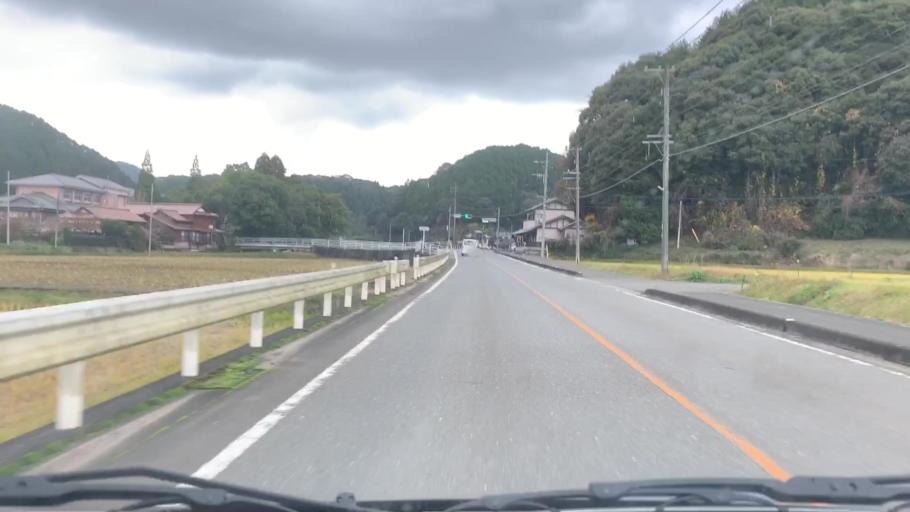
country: JP
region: Saga Prefecture
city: Ureshinomachi-shimojuku
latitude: 33.1379
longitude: 129.9731
